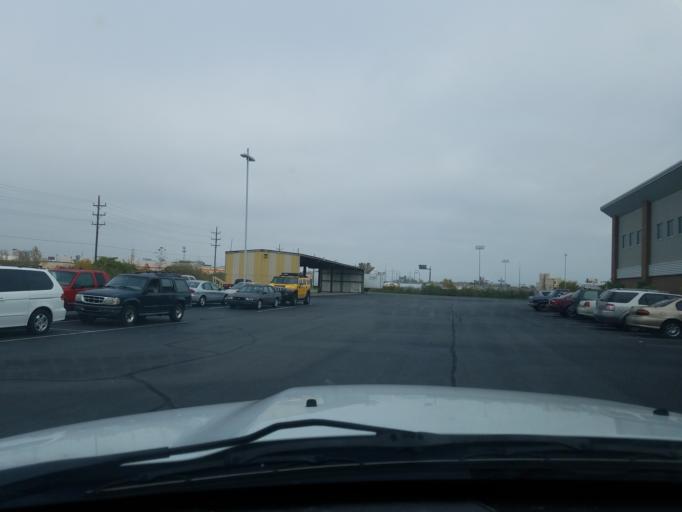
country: US
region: Indiana
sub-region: Clark County
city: Clarksville
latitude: 38.3122
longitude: -85.7585
